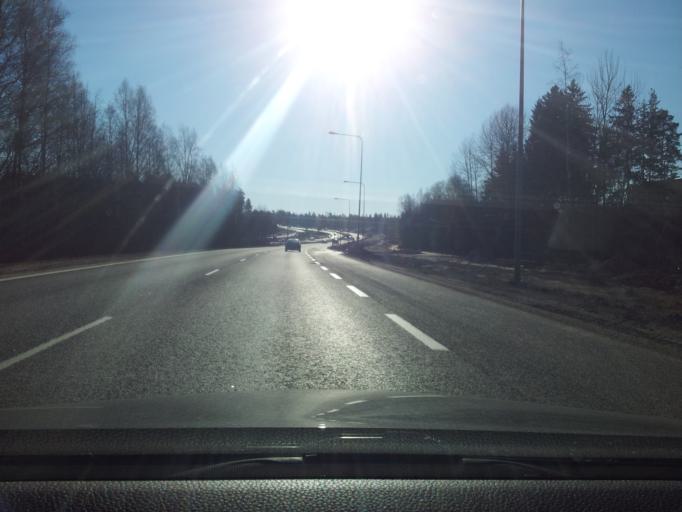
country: FI
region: Uusimaa
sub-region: Helsinki
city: Vantaa
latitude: 60.2344
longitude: 25.0468
